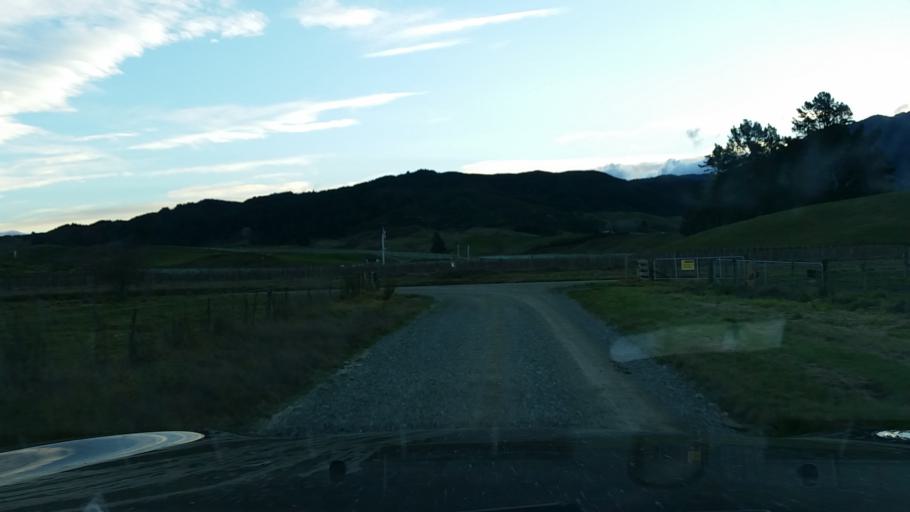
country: NZ
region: Marlborough
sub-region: Marlborough District
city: Blenheim
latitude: -41.5142
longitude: 173.5863
